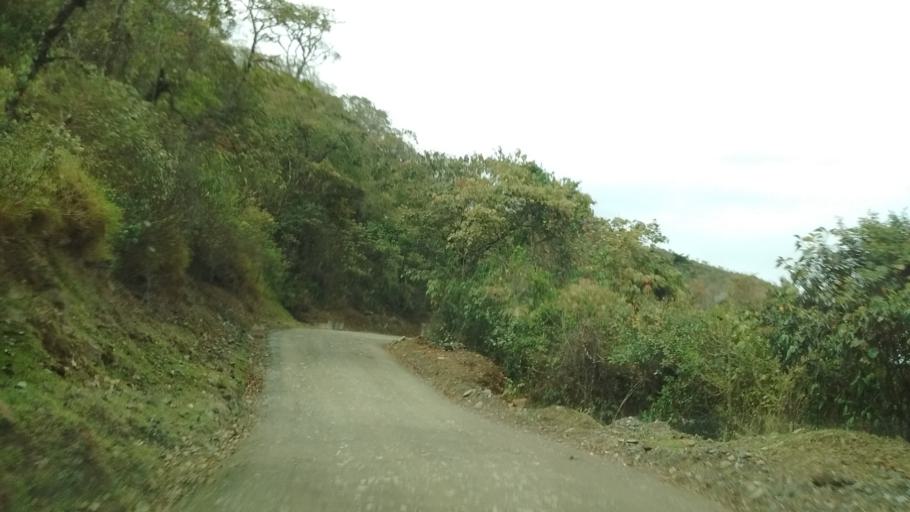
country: CO
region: Cauca
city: Almaguer
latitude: 1.8540
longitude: -76.9489
